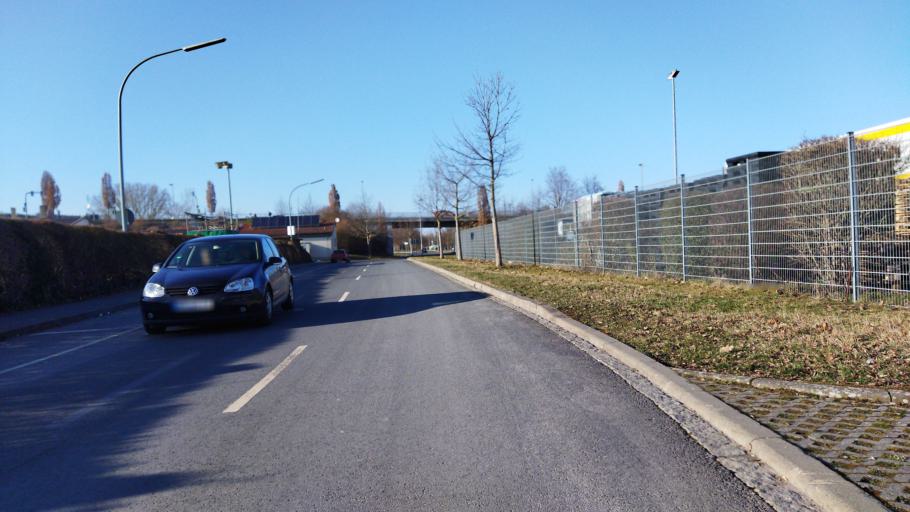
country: DE
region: Bavaria
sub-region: Regierungsbezirk Unterfranken
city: Kitzingen
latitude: 49.7443
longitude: 10.1641
